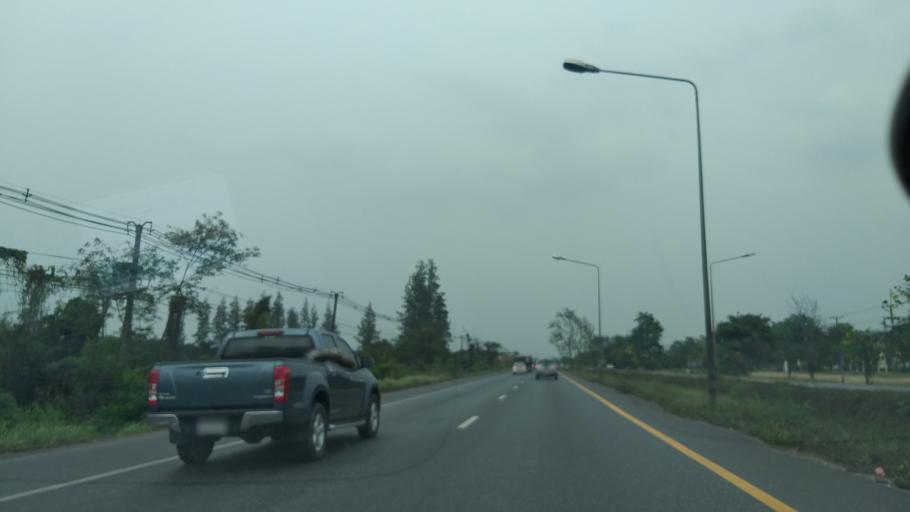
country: TH
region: Chon Buri
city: Ko Chan
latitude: 13.3022
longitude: 101.2625
